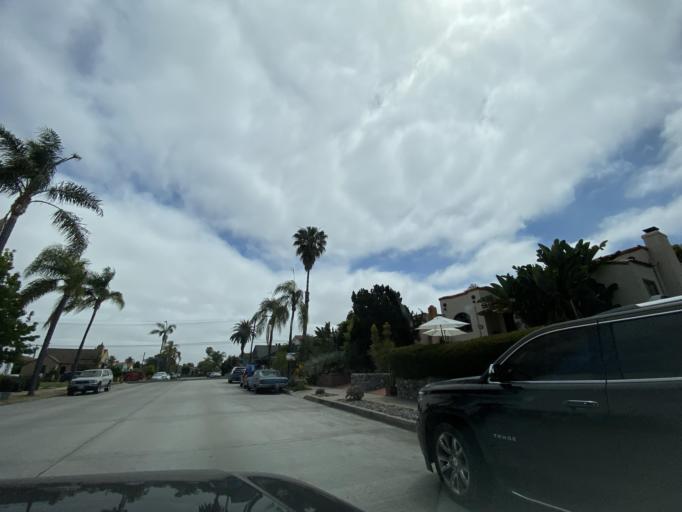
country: US
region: California
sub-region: San Diego County
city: San Diego
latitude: 32.7425
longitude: -117.1229
